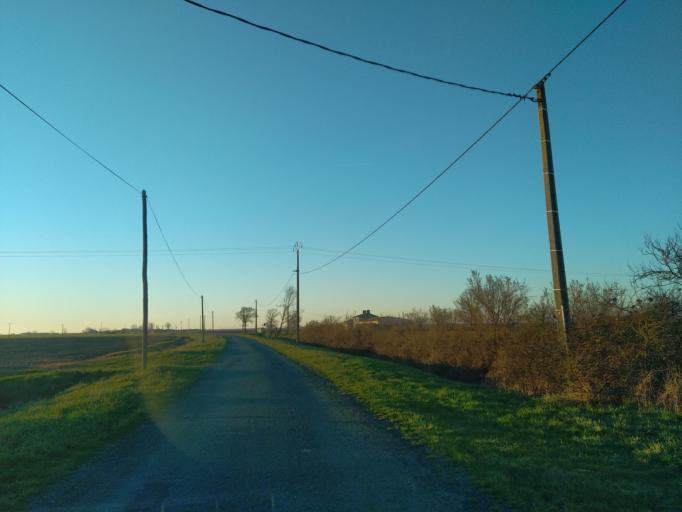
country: FR
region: Pays de la Loire
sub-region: Departement de la Vendee
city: Triaize
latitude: 46.3700
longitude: -1.2637
